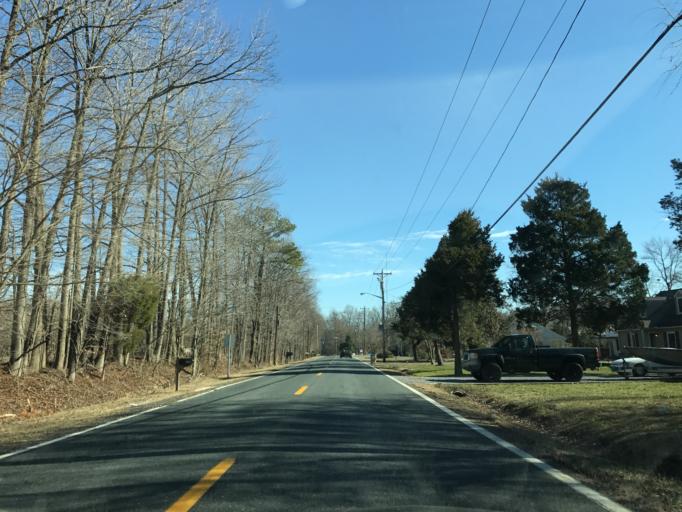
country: US
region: Maryland
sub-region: Queen Anne's County
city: Grasonville
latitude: 38.9862
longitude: -76.1502
